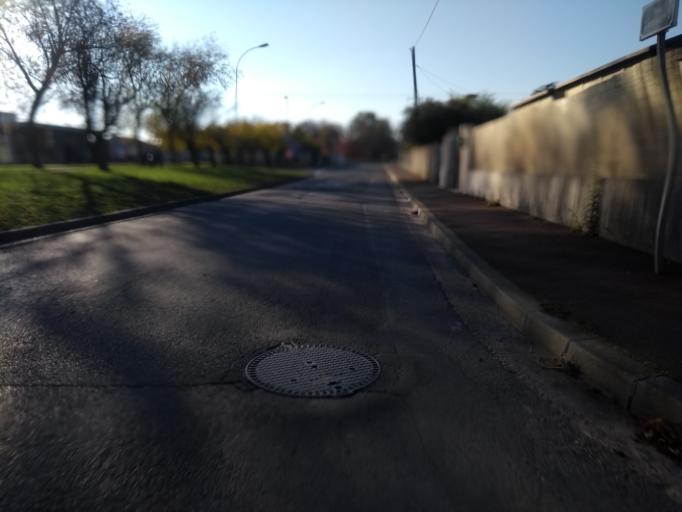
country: FR
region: Aquitaine
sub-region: Departement de la Gironde
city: Gradignan
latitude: 44.7651
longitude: -0.5843
